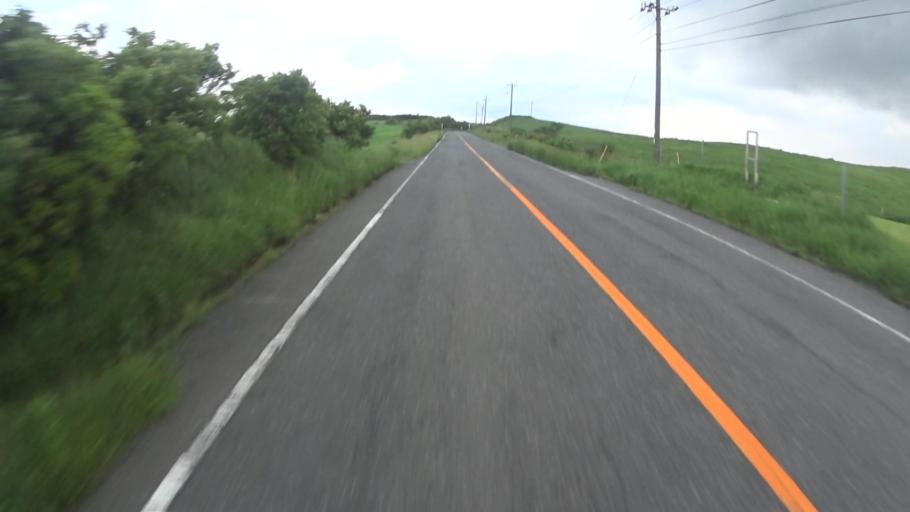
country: JP
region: Kumamoto
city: Aso
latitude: 32.9748
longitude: 131.0111
